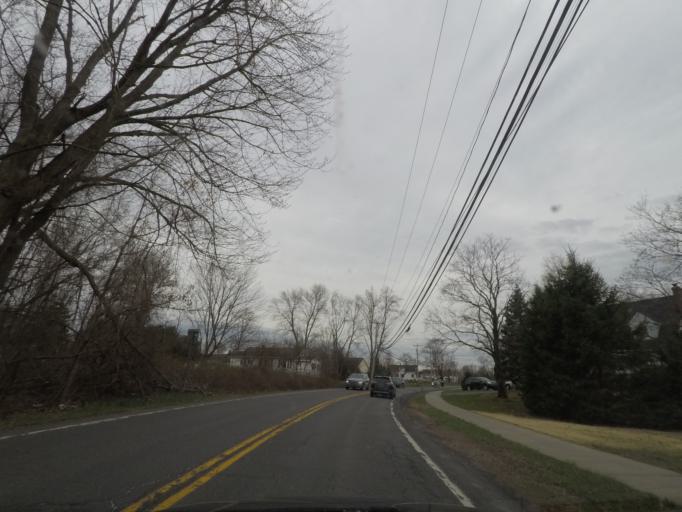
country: US
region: New York
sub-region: Albany County
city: Delmar
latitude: 42.6064
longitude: -73.8184
